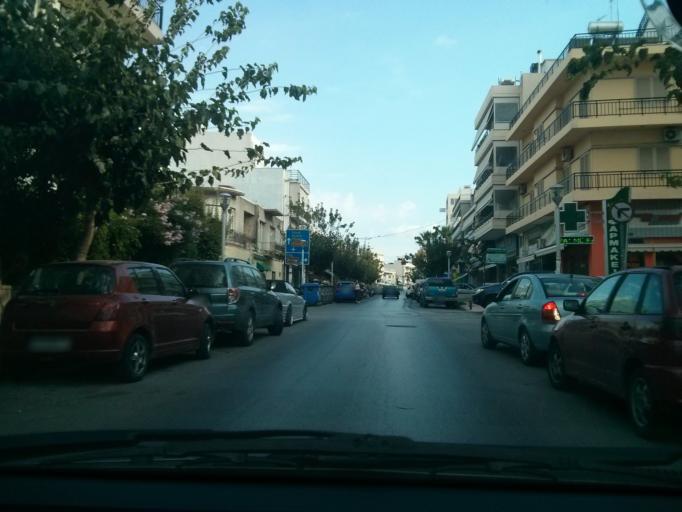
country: GR
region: Crete
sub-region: Nomos Irakleiou
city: Irakleion
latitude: 35.3296
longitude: 25.1369
